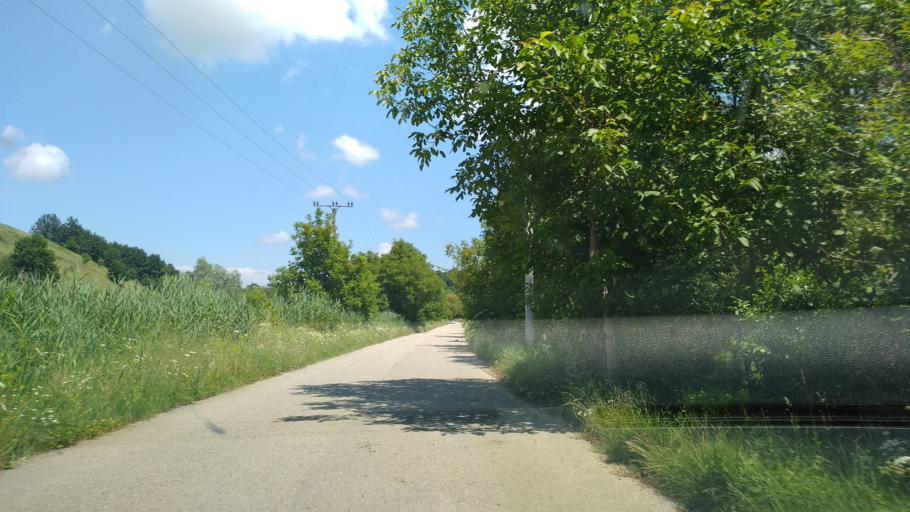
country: RO
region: Hunedoara
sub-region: Comuna Bosorod
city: Bosorod
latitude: 45.7098
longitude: 23.1135
